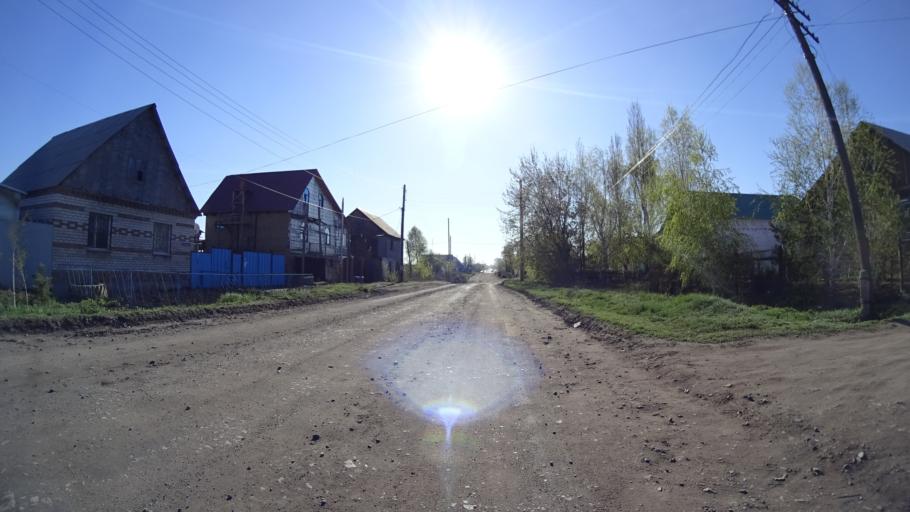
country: RU
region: Chelyabinsk
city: Troitsk
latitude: 54.0960
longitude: 61.5963
